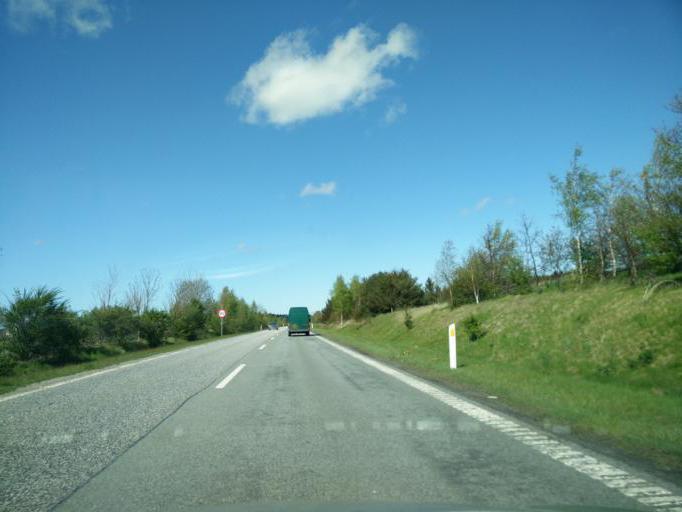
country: DK
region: Capital Region
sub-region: Gribskov Kommune
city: Helsinge
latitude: 55.9850
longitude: 12.2445
